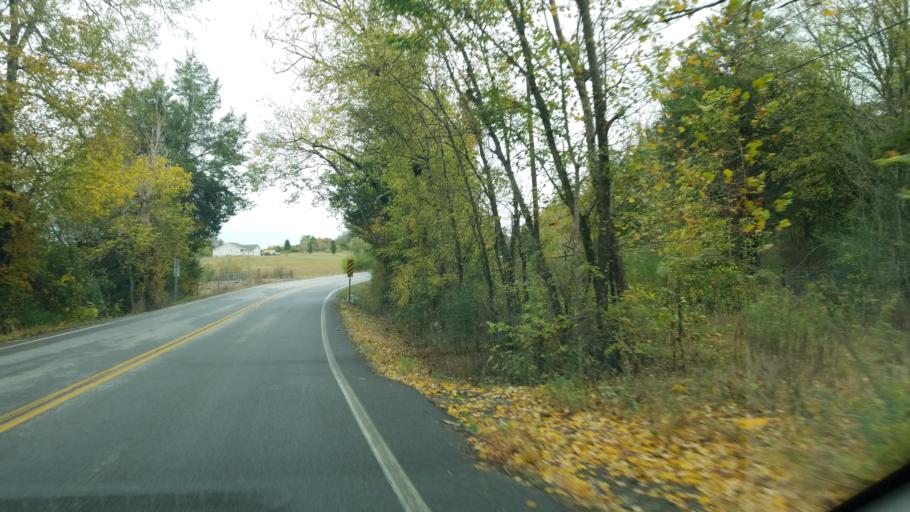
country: US
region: Tennessee
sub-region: Bradley County
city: Hopewell
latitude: 35.2290
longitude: -84.9980
